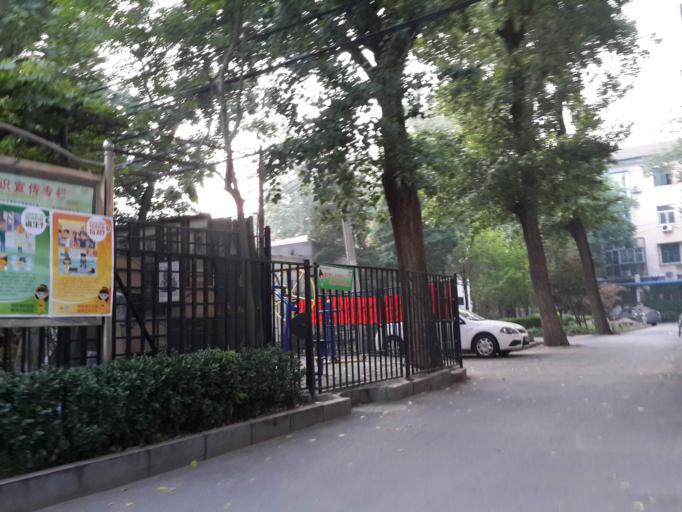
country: CN
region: Beijing
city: Chaowai
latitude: 39.9338
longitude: 116.4462
